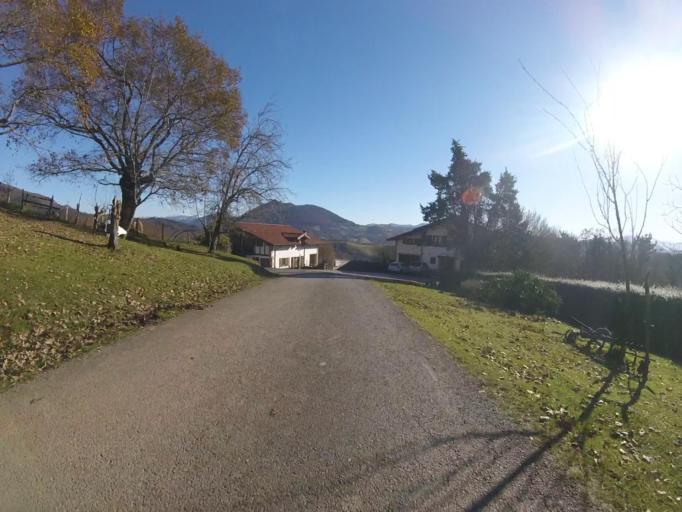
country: ES
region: Navarre
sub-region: Provincia de Navarra
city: Bera
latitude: 43.2966
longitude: -1.6596
